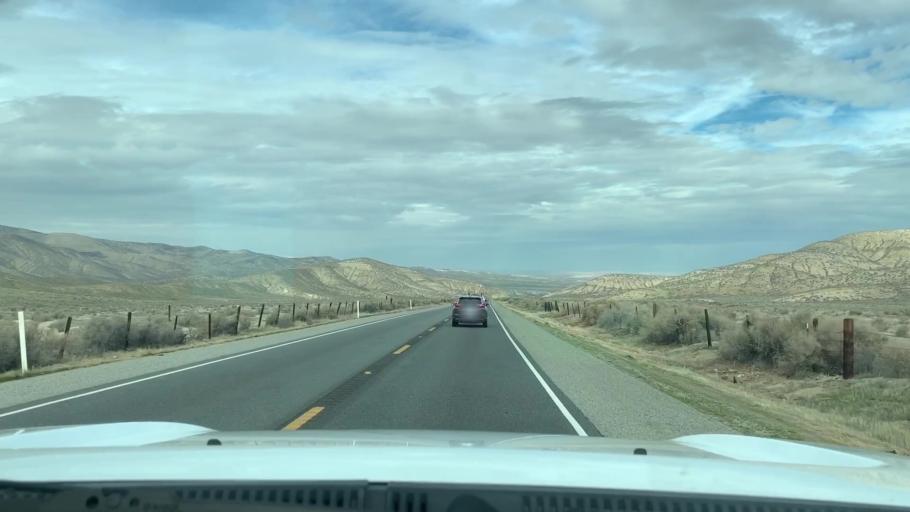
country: US
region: California
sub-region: Kern County
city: Maricopa
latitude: 35.0190
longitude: -119.4159
